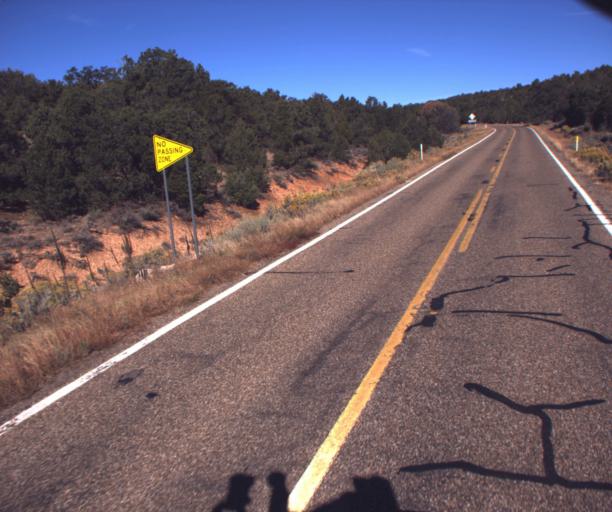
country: US
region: Arizona
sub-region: Coconino County
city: Fredonia
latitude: 36.7350
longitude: -112.0979
